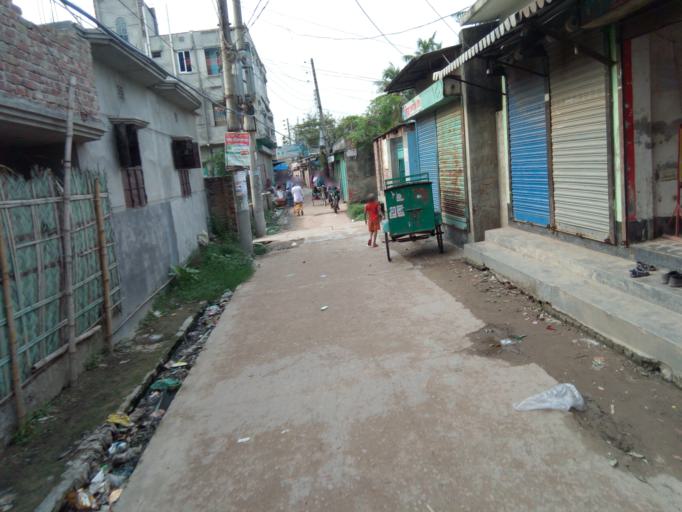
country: BD
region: Dhaka
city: Paltan
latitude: 23.7087
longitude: 90.4972
